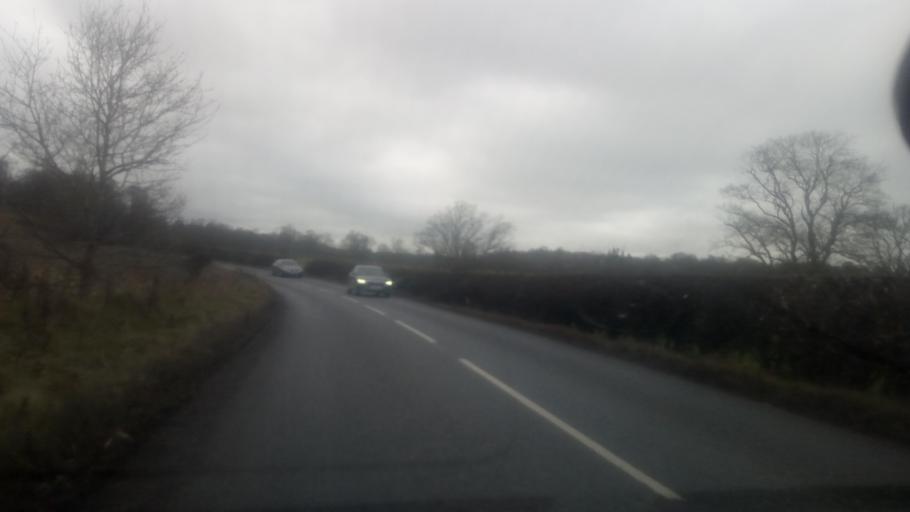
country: GB
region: Scotland
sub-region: The Scottish Borders
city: Kelso
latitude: 55.5976
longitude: -2.4560
